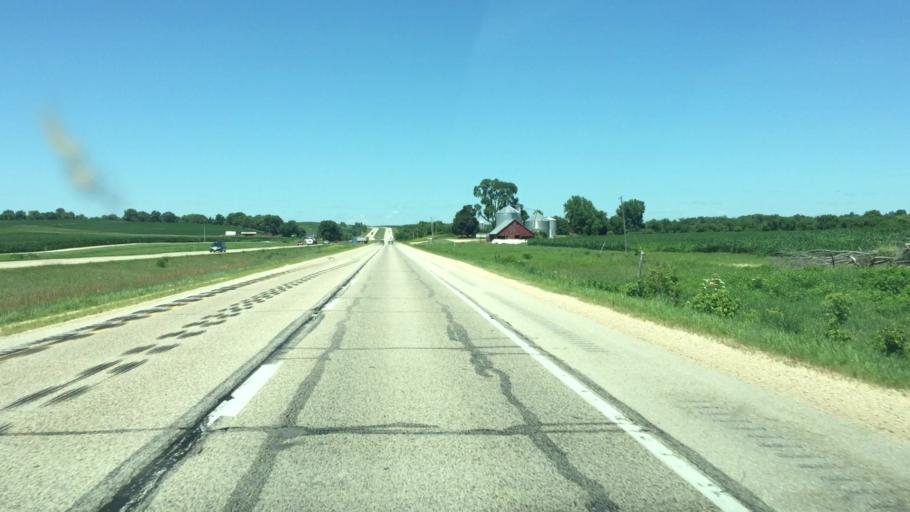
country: US
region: Iowa
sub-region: Jackson County
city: Maquoketa
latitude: 42.1748
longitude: -90.6732
